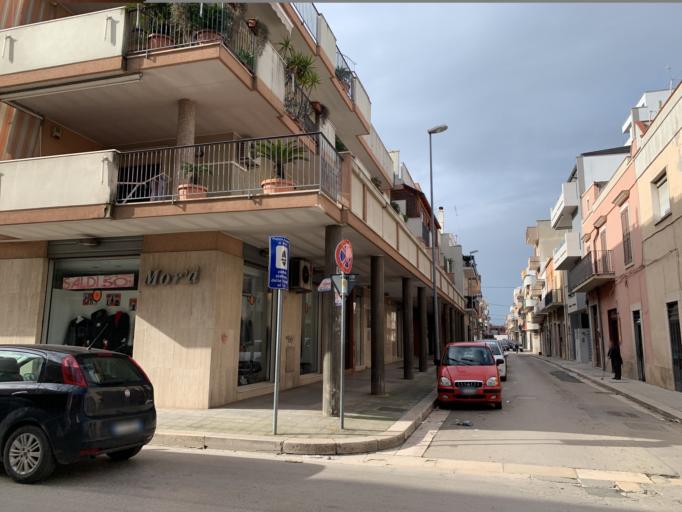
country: IT
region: Apulia
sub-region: Provincia di Barletta - Andria - Trani
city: Andria
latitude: 41.2337
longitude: 16.2948
